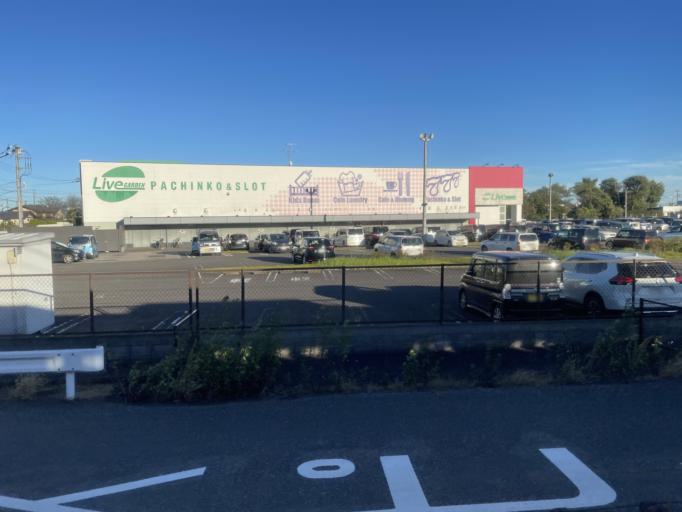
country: JP
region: Saitama
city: Satte
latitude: 36.0944
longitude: 139.7188
